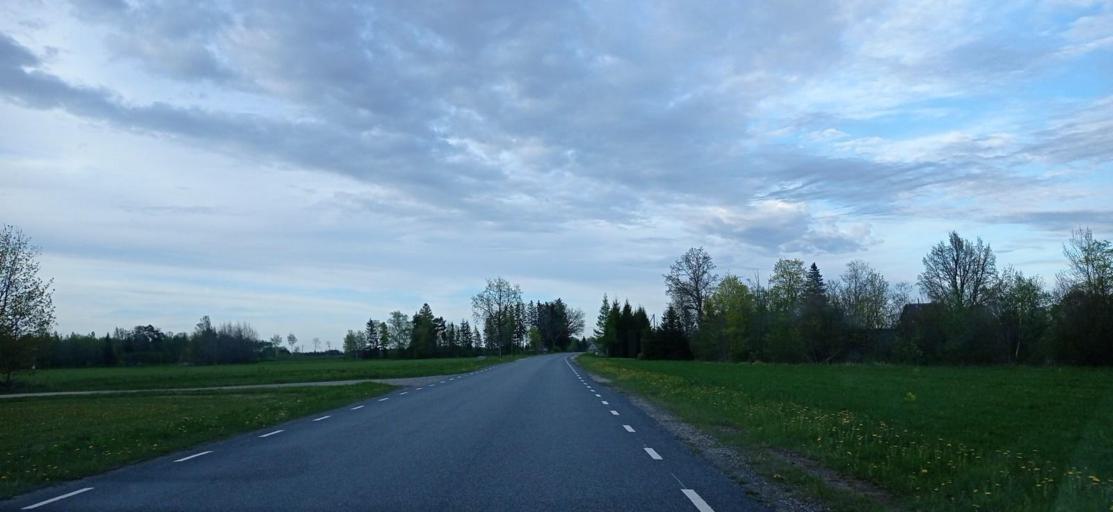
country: EE
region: Paernumaa
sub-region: Tootsi vald
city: Tootsi
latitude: 58.5318
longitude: 24.7120
